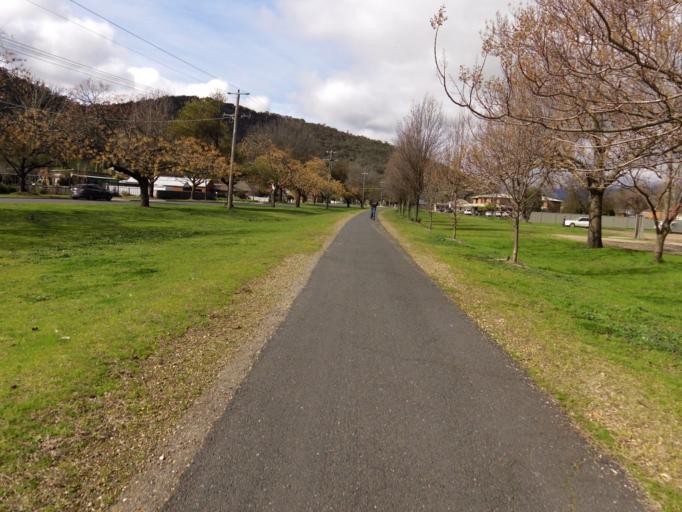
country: AU
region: Victoria
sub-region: Wangaratta
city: Wangaratta
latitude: -36.5610
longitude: 146.7272
